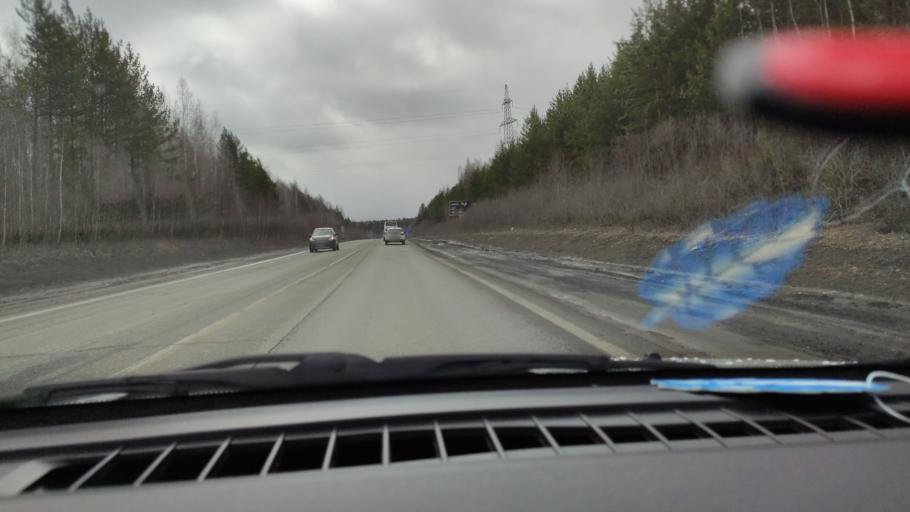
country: RU
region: Sverdlovsk
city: Talitsa
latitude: 56.8522
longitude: 60.0584
